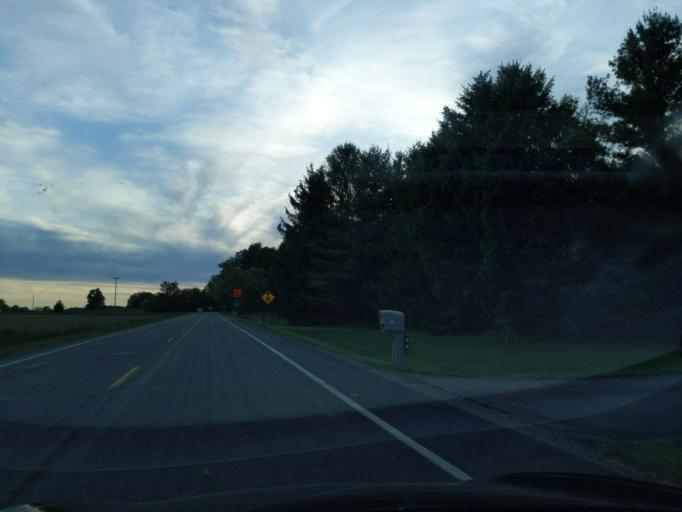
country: US
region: Michigan
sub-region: Ingham County
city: Mason
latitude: 42.6007
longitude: -84.3547
